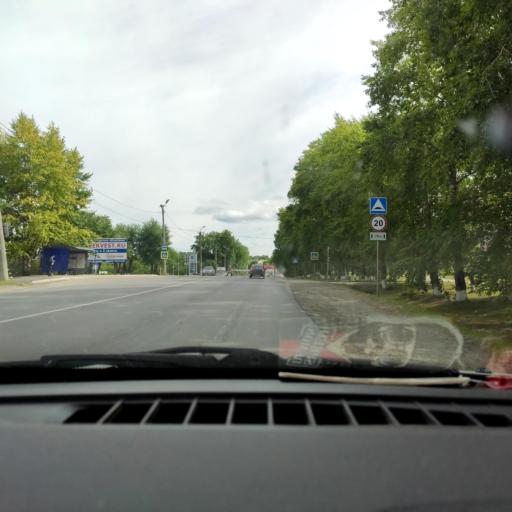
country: RU
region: Perm
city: Chusovoy
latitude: 58.2752
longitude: 57.8152
